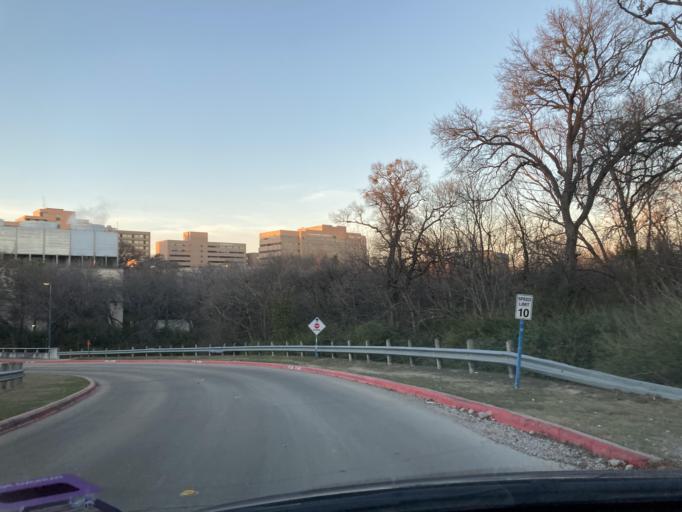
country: US
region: Texas
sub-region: Dallas County
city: University Park
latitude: 32.8784
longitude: -96.7616
